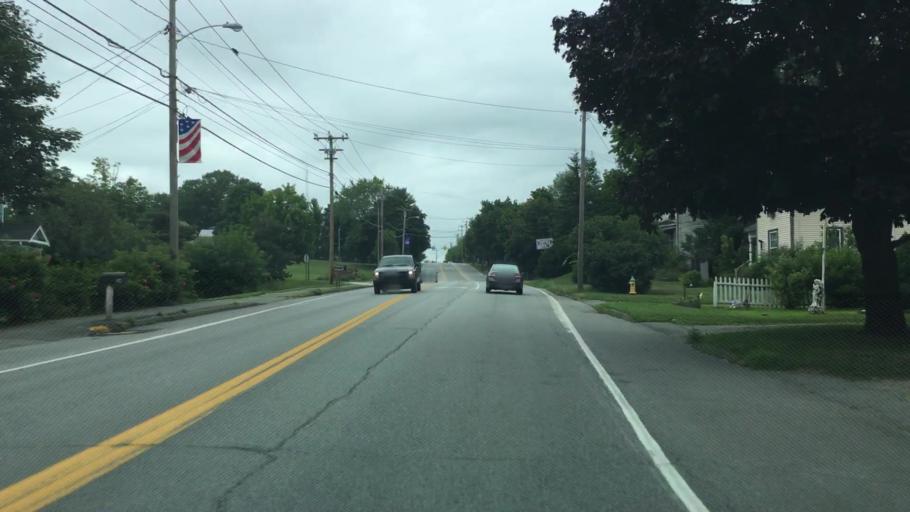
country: US
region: Maine
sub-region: Penobscot County
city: Hampden
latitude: 44.7372
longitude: -68.8401
